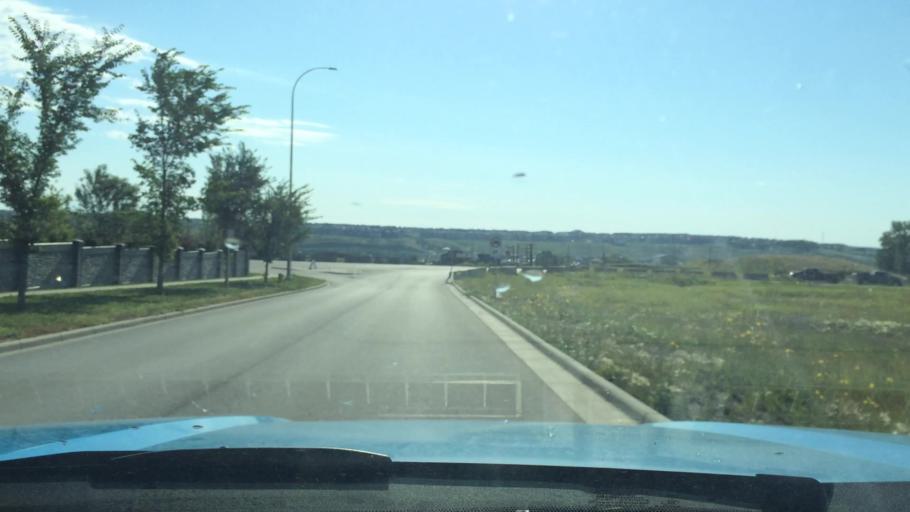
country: CA
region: Alberta
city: Calgary
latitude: 51.1759
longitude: -114.1426
